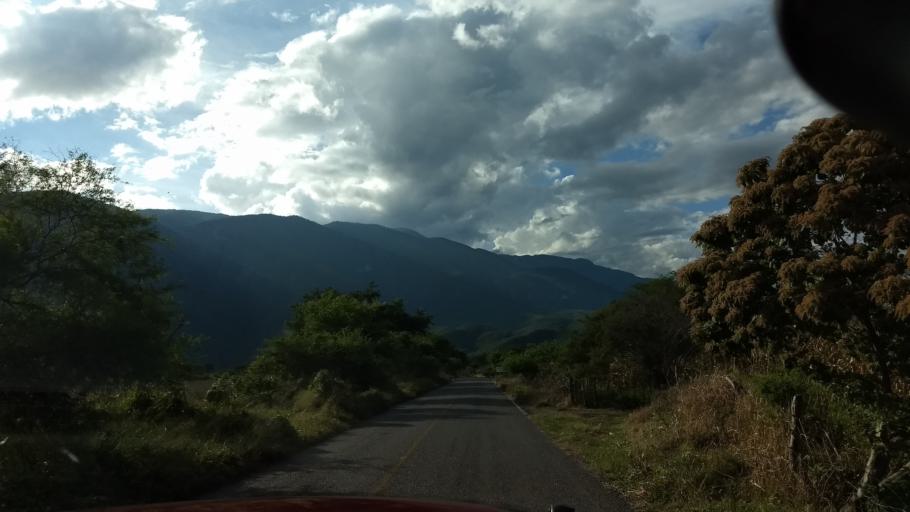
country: MX
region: Colima
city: Suchitlan
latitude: 19.4487
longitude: -103.8160
